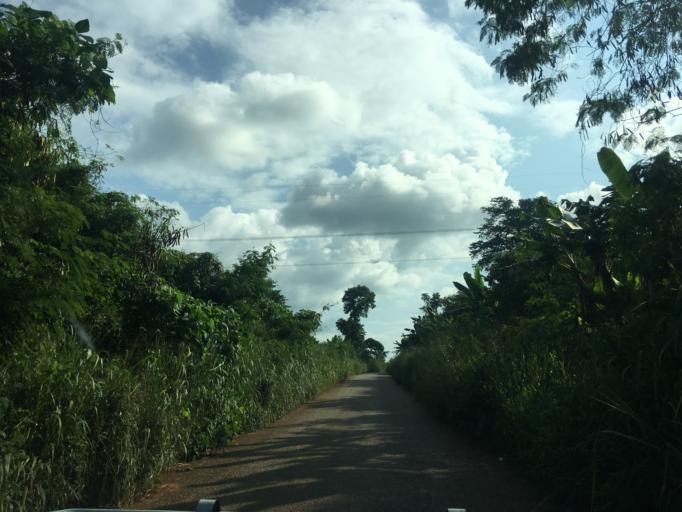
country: GH
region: Western
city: Bibiani
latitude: 6.7938
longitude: -2.5321
